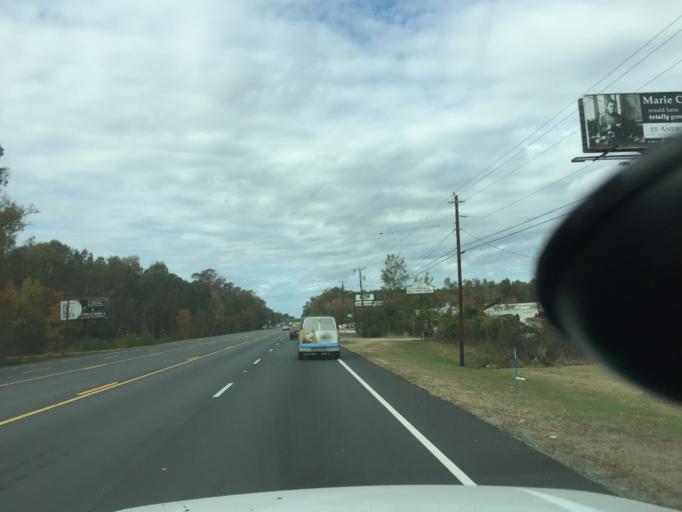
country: US
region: Georgia
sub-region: Chatham County
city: Garden City
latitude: 32.0911
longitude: -81.1892
